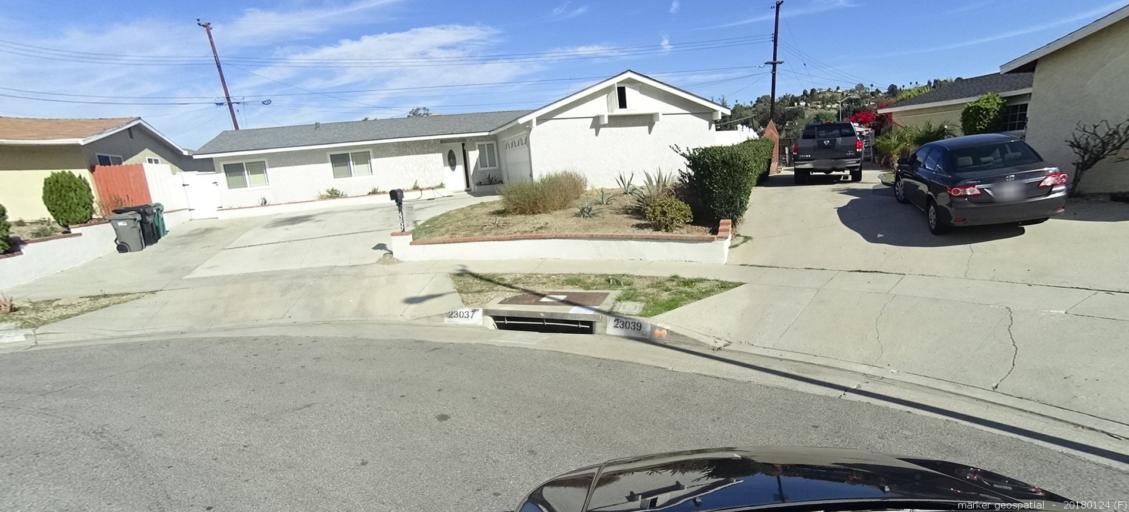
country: US
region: California
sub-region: Los Angeles County
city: Diamond Bar
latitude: 34.0285
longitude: -117.8132
